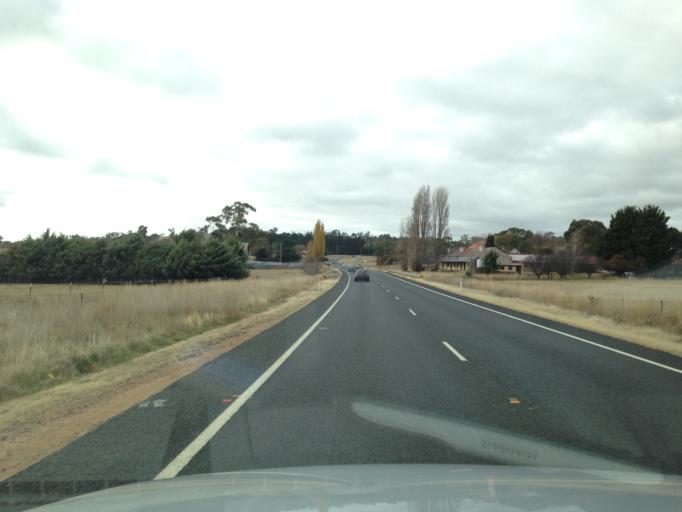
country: AU
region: New South Wales
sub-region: Cooma-Monaro
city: Cooma
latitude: -36.2434
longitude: 149.0607
